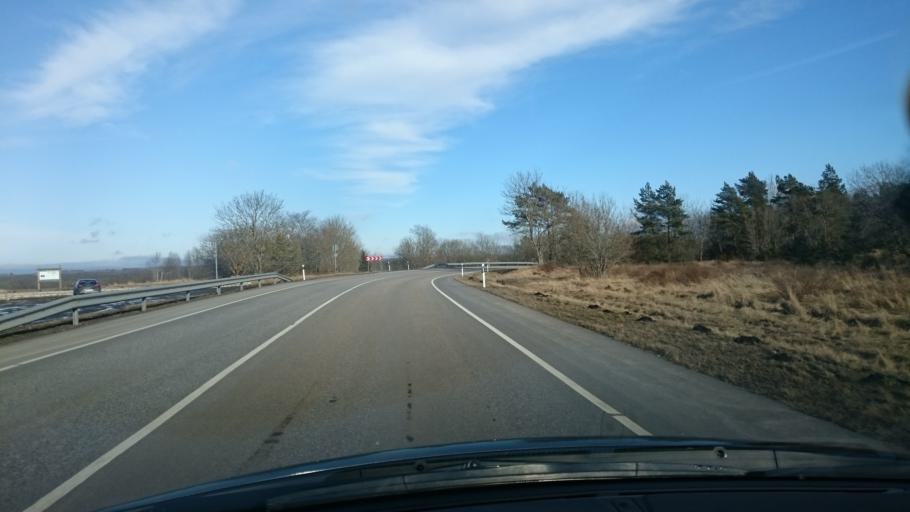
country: EE
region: Harju
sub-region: Keila linn
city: Keila
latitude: 59.4216
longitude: 24.3298
